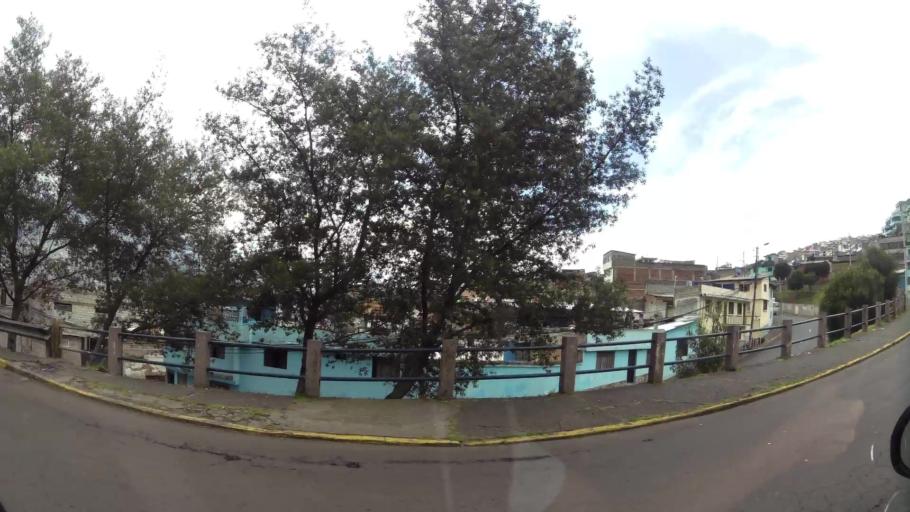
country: EC
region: Pichincha
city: Quito
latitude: -0.2520
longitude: -78.5148
